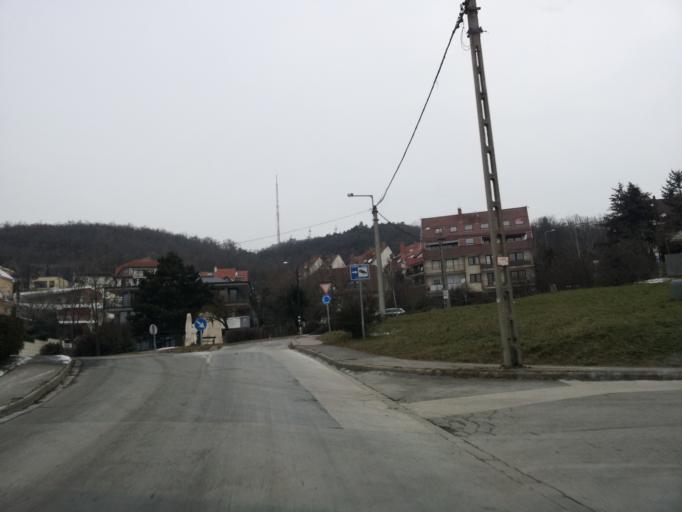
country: HU
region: Budapest
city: Budapest XII. keruelet
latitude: 47.4873
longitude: 18.9903
